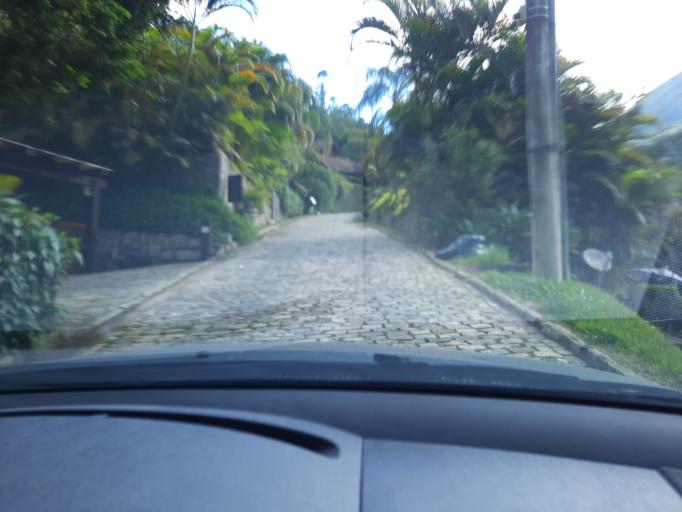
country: BR
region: Rio de Janeiro
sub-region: Petropolis
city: Petropolis
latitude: -22.4413
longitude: -43.1731
